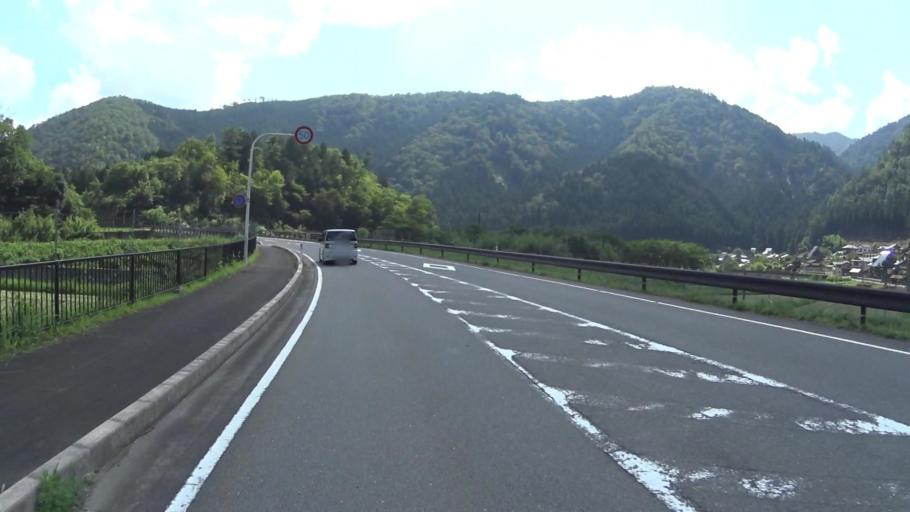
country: JP
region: Kyoto
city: Maizuru
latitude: 35.3127
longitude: 135.5547
